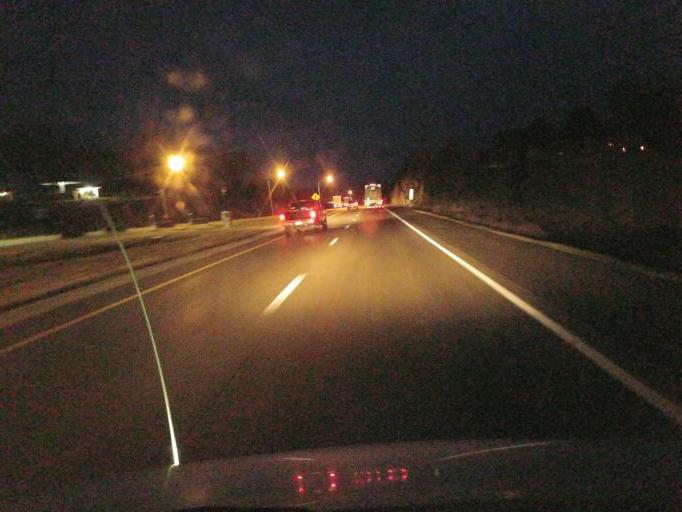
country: US
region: Missouri
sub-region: Franklin County
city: Saint Clair
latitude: 38.3165
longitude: -91.0478
